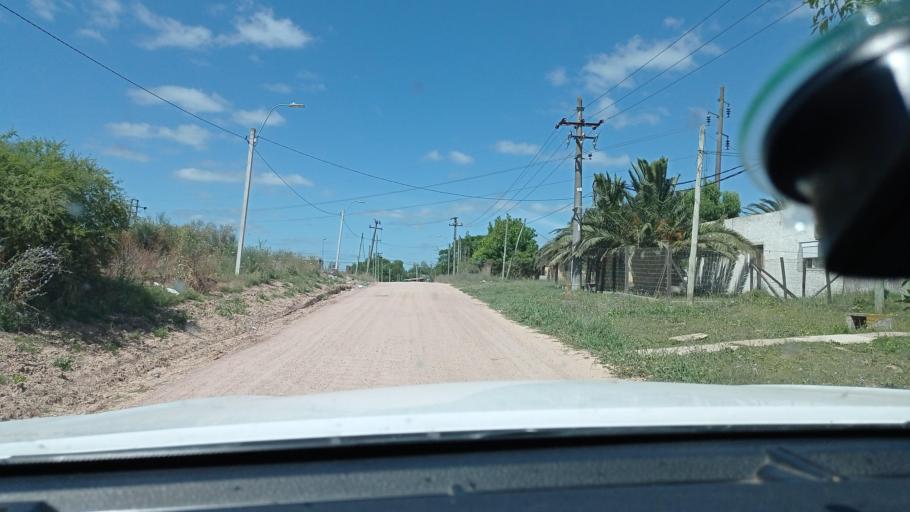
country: UY
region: Canelones
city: Pando
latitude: -34.7193
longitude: -55.9710
